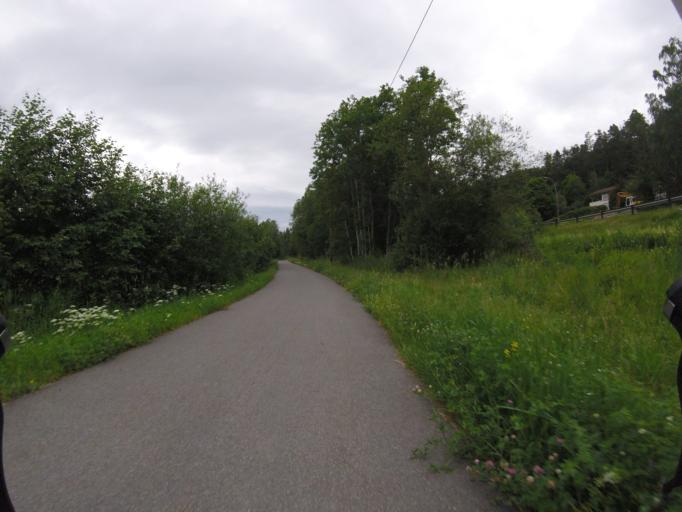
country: NO
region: Akershus
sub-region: Skedsmo
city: Lillestrom
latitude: 59.9770
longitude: 11.0217
